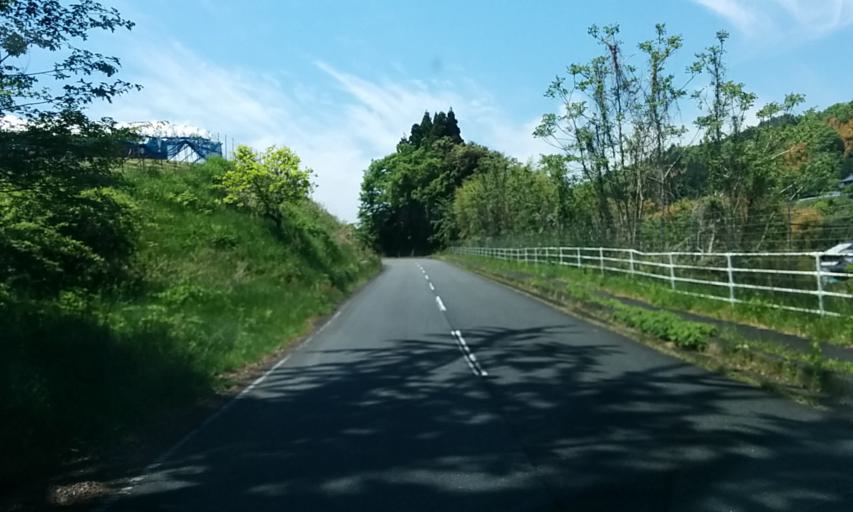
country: JP
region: Kyoto
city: Ayabe
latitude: 35.2094
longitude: 135.2838
